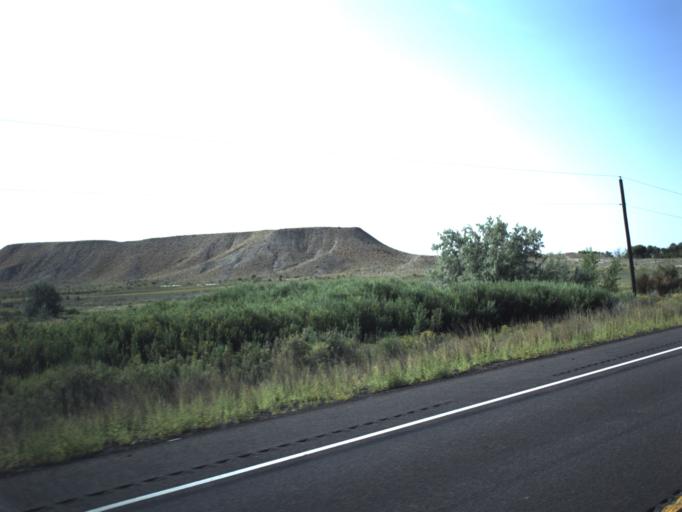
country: US
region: Utah
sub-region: Emery County
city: Huntington
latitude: 39.2722
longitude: -110.9784
